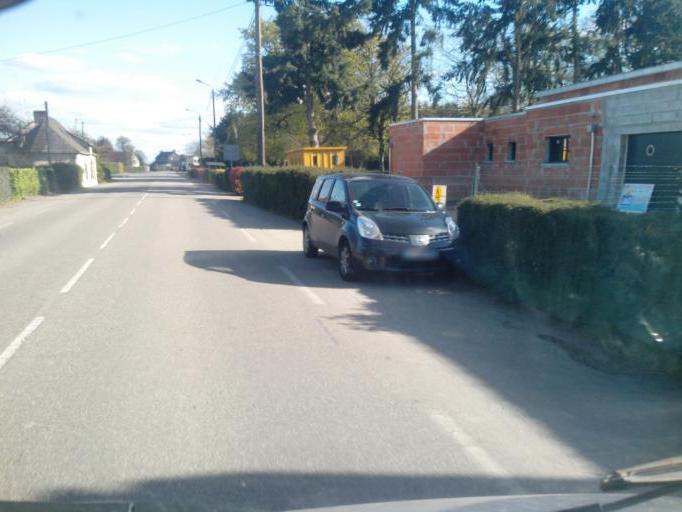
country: FR
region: Brittany
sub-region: Departement d'Ille-et-Vilaine
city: Guipry
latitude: 47.8307
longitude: -1.8479
